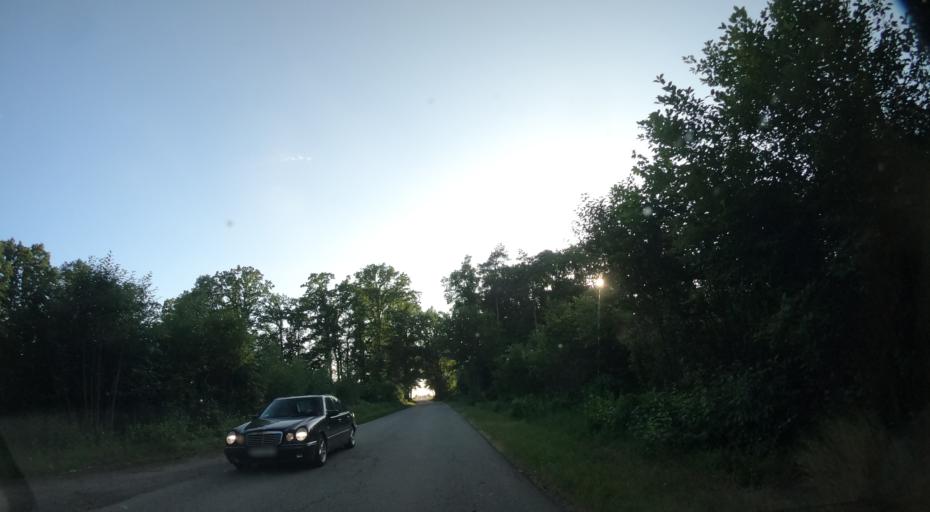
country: PL
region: Lubusz
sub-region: Powiat gorzowski
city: Klodawa
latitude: 52.7801
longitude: 15.1296
